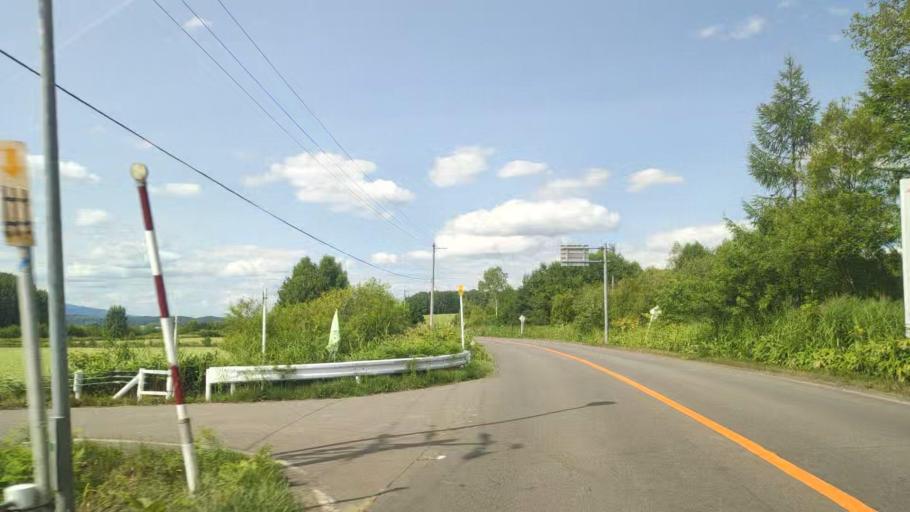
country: JP
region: Hokkaido
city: Nayoro
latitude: 44.2762
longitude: 142.4231
